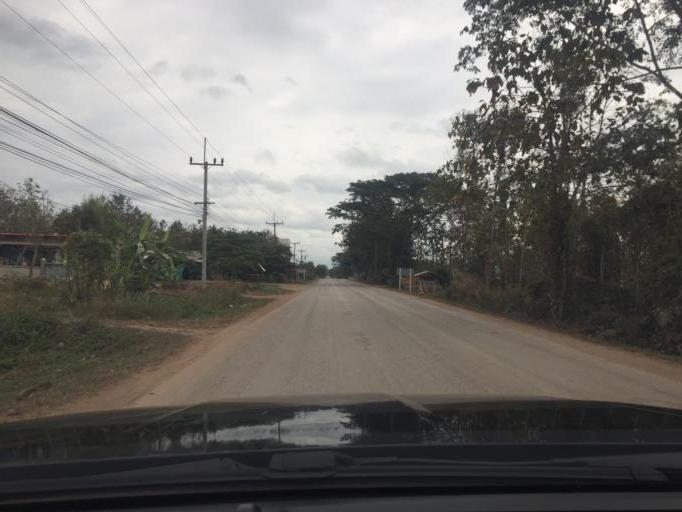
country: TH
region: Phayao
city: Pong
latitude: 19.1673
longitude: 100.3074
